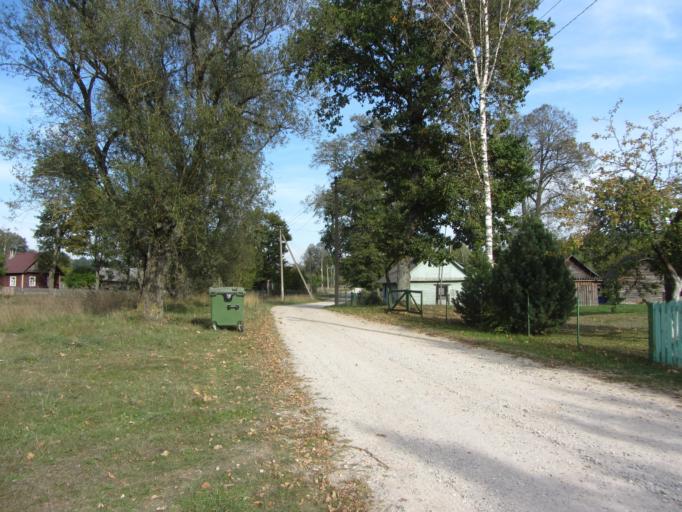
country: LT
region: Alytaus apskritis
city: Druskininkai
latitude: 53.9987
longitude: 24.2908
